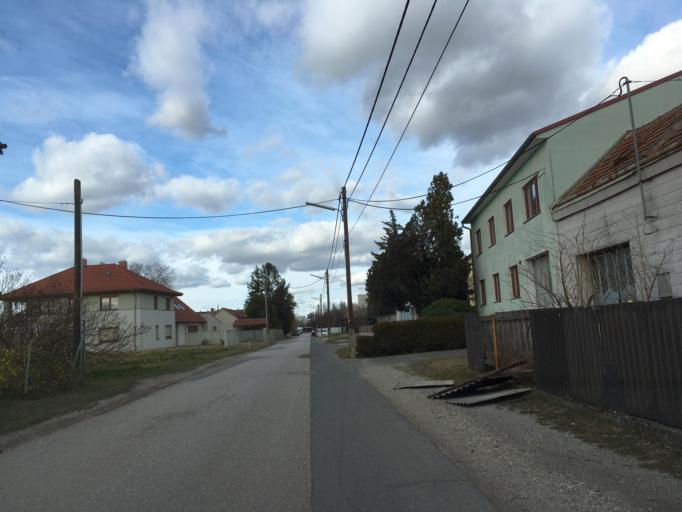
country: AT
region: Lower Austria
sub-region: Politischer Bezirk Ganserndorf
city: Gross-Enzersdorf
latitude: 48.2123
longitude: 16.5037
